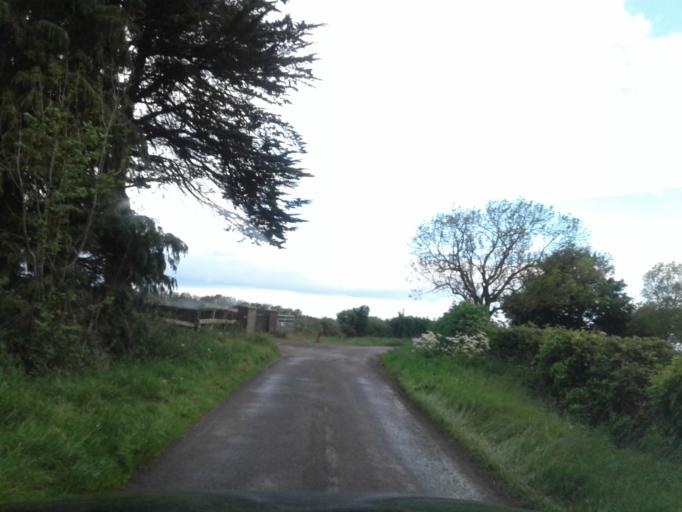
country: IE
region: Leinster
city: Ballymun
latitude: 53.4322
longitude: -6.2898
